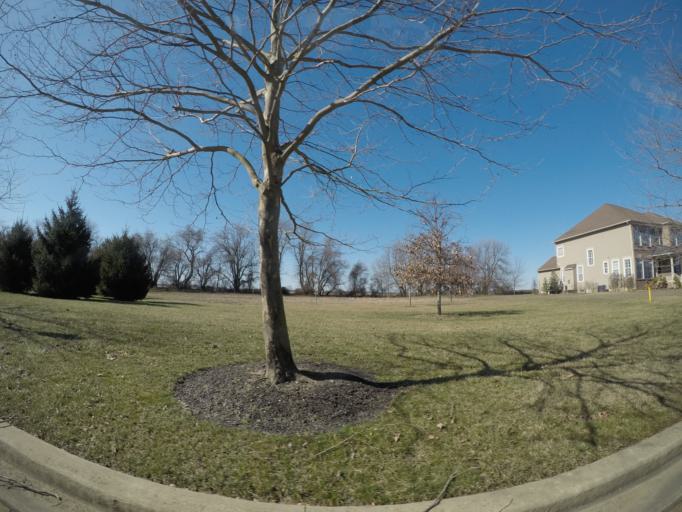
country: US
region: Delaware
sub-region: New Castle County
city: Middletown
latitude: 39.5054
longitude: -75.6664
